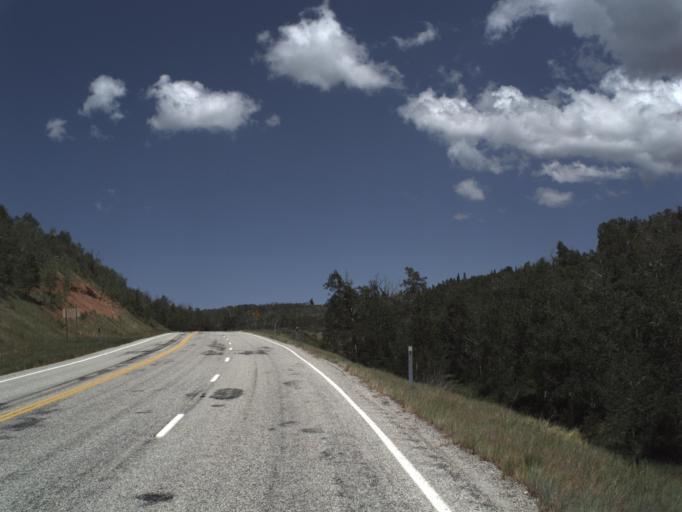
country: US
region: Utah
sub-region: Weber County
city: Wolf Creek
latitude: 41.4174
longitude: -111.5690
